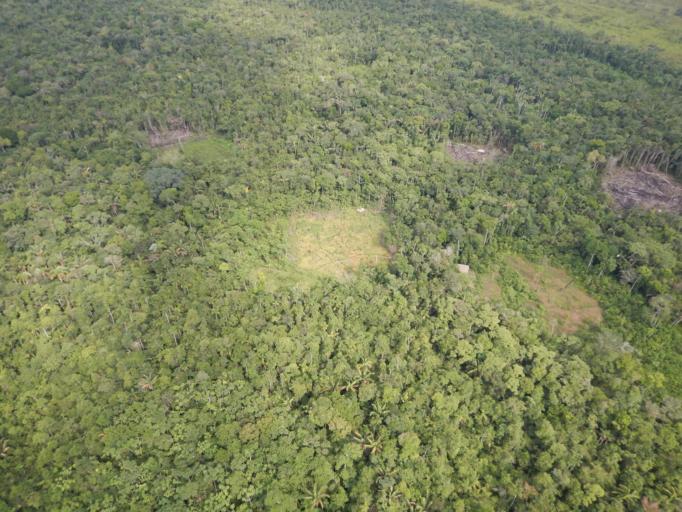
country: BO
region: Cochabamba
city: Chimore
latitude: -16.9462
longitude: -64.9755
